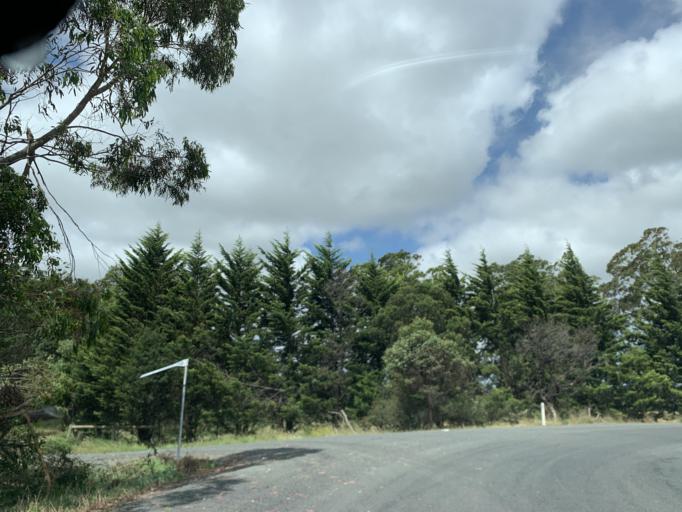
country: AU
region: Victoria
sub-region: Latrobe
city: Traralgon
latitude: -38.1139
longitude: 146.5558
